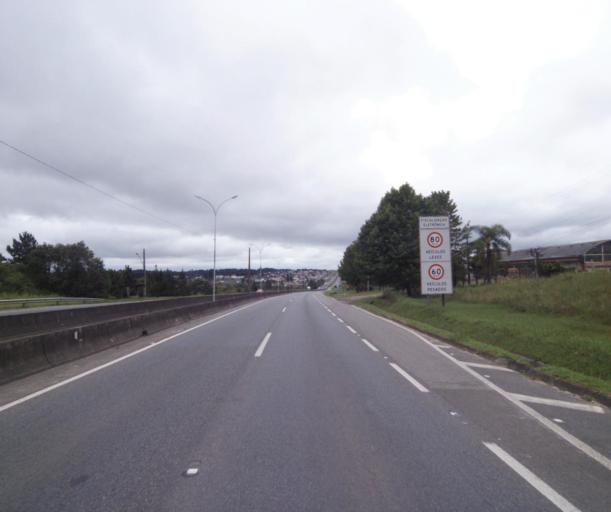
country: BR
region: Parana
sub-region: Quatro Barras
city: Quatro Barras
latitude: -25.3641
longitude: -49.0857
